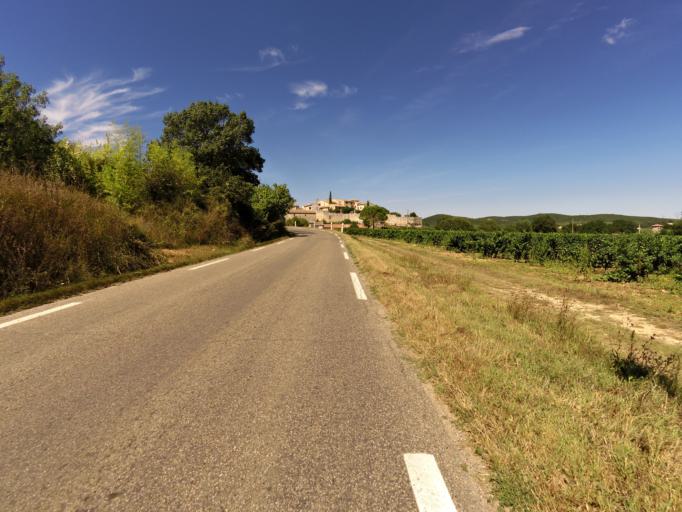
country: FR
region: Languedoc-Roussillon
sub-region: Departement du Gard
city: Sommieres
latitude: 43.8340
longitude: 4.0639
